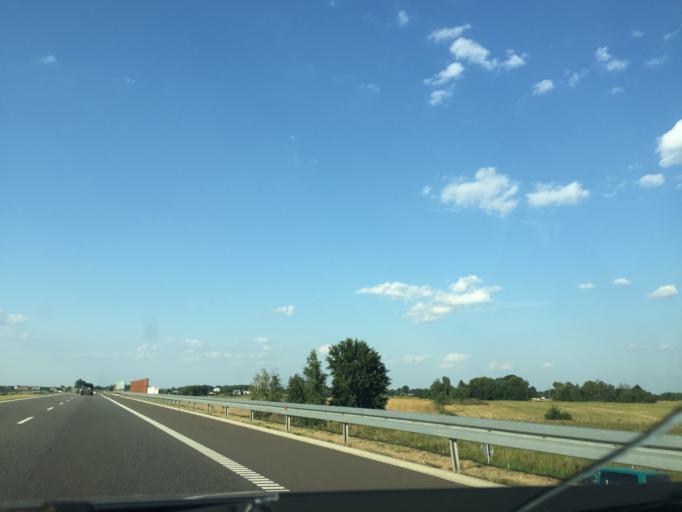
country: PL
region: Masovian Voivodeship
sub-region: Powiat radomski
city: Zakrzew
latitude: 51.4639
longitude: 21.0471
